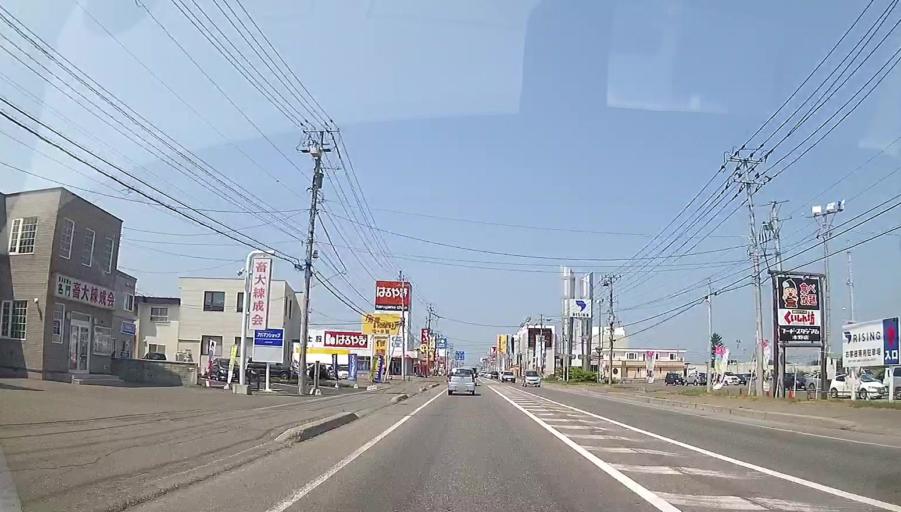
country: JP
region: Hokkaido
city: Otofuke
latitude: 42.9549
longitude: 143.2057
